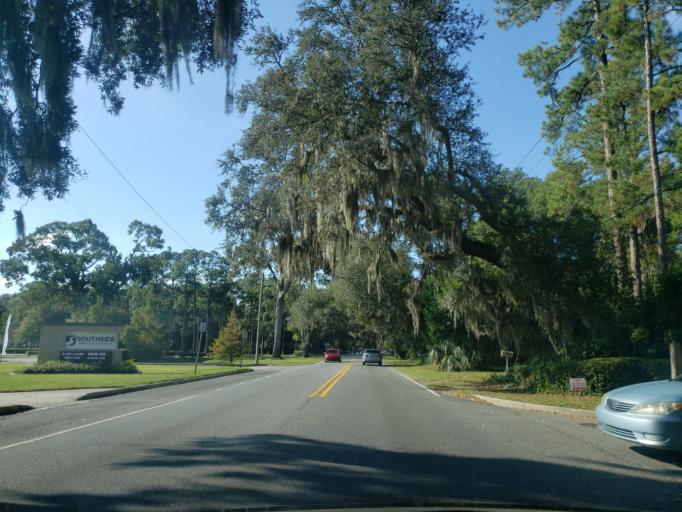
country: US
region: Georgia
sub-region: Chatham County
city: Thunderbolt
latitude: 32.0174
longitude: -81.0761
